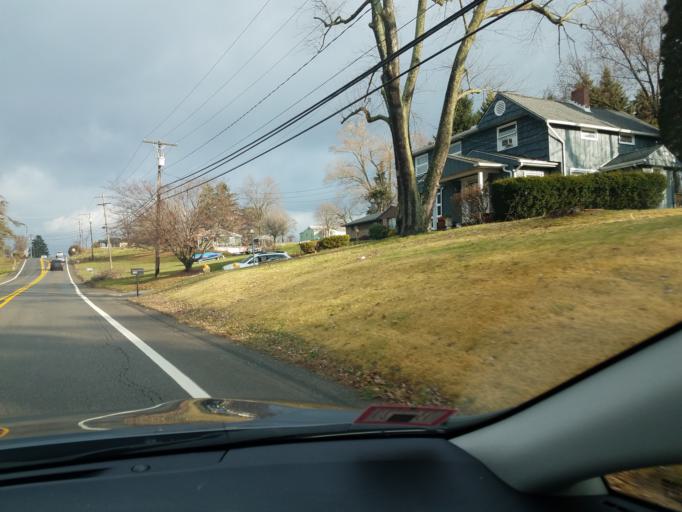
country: US
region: Pennsylvania
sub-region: Allegheny County
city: Franklin Park
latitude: 40.6102
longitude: -80.0997
